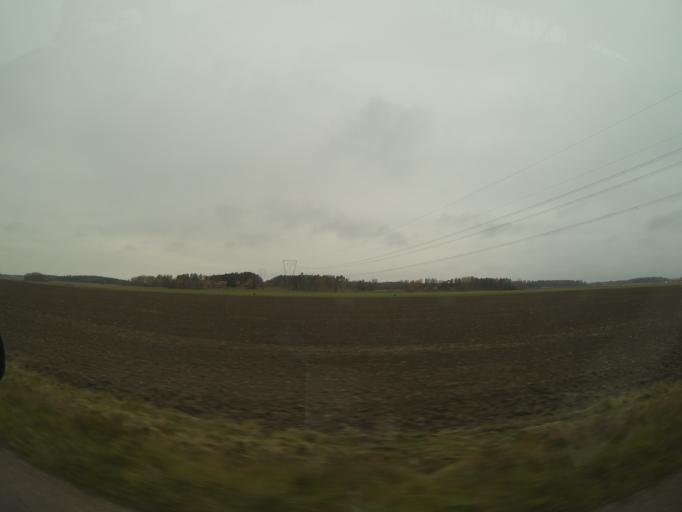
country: SE
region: Vaestmanland
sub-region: Kopings Kommun
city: Koping
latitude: 59.5497
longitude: 16.1082
